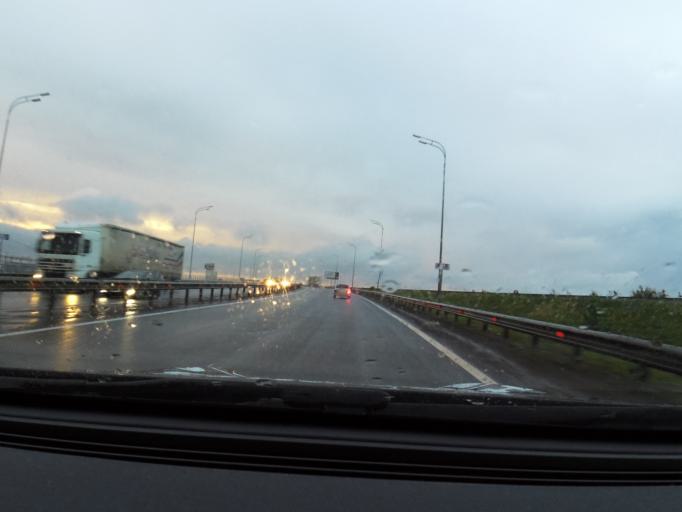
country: RU
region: Tatarstan
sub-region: Tukayevskiy Rayon
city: Naberezhnyye Chelny
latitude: 55.6890
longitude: 52.2832
